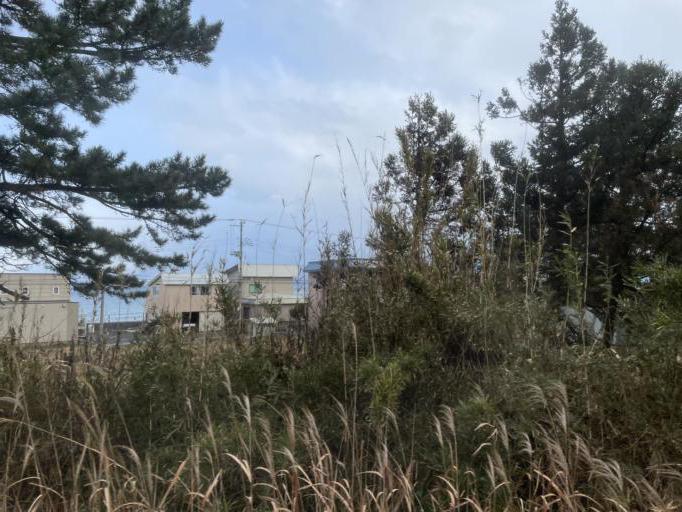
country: JP
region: Aomori
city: Aomori Shi
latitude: 41.0190
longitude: 140.6474
